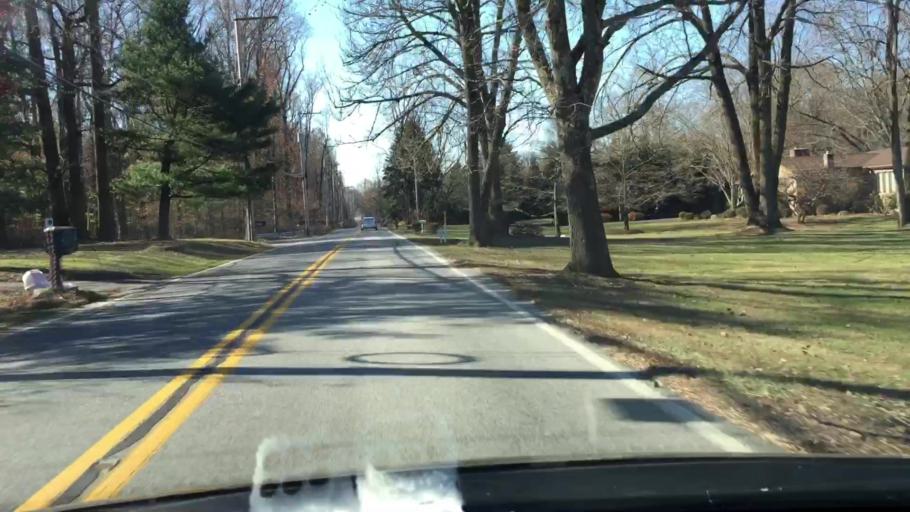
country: US
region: Pennsylvania
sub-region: Delaware County
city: Chester Heights
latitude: 39.8534
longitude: -75.5004
